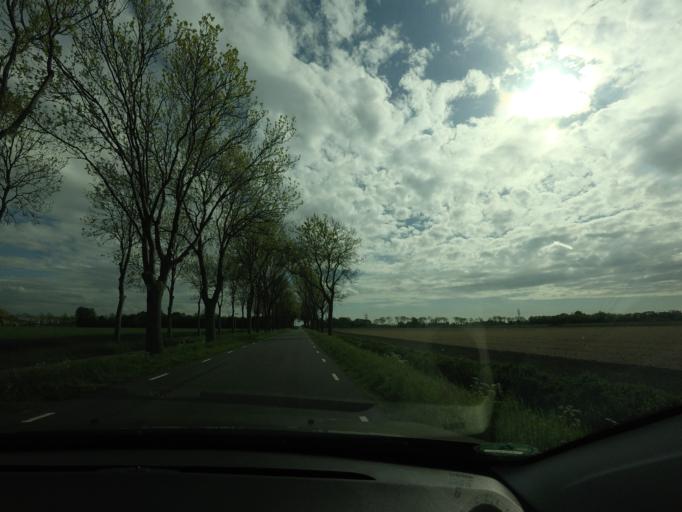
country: NL
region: North Holland
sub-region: Gemeente Beemster
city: Halfweg
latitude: 52.5271
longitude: 4.8999
